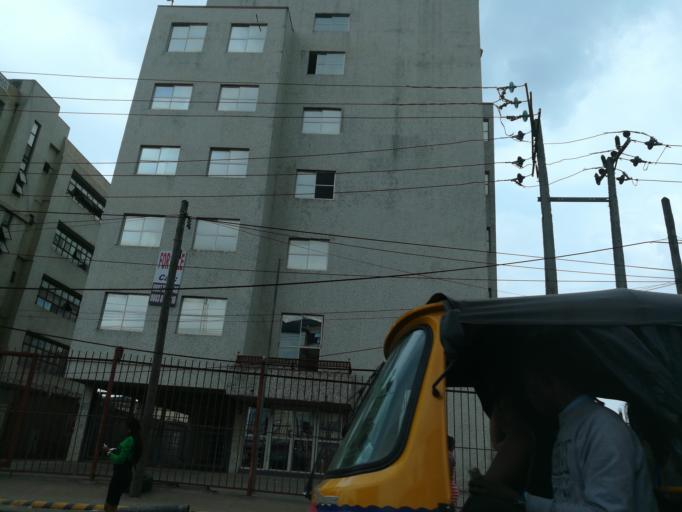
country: NG
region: Lagos
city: Ikeja
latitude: 6.5987
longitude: 3.3400
